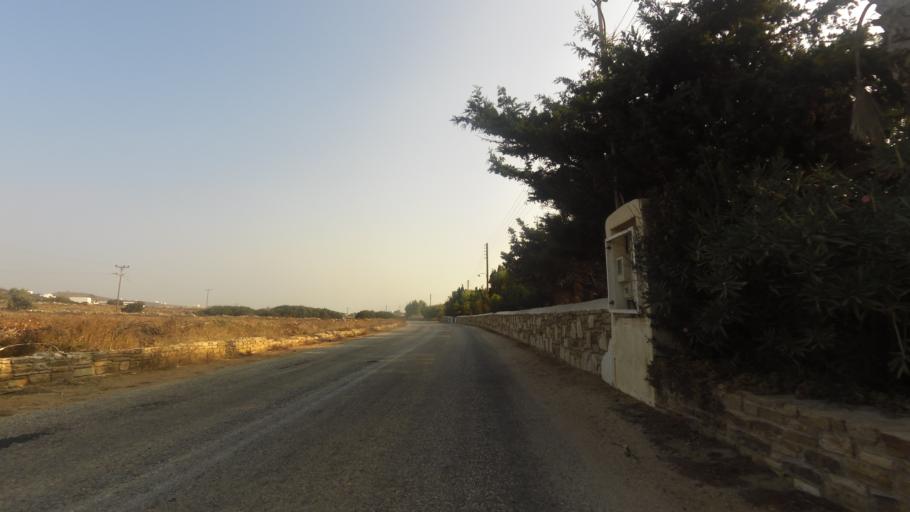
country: GR
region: South Aegean
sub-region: Nomos Kykladon
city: Antiparos
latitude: 37.0201
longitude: 25.0765
